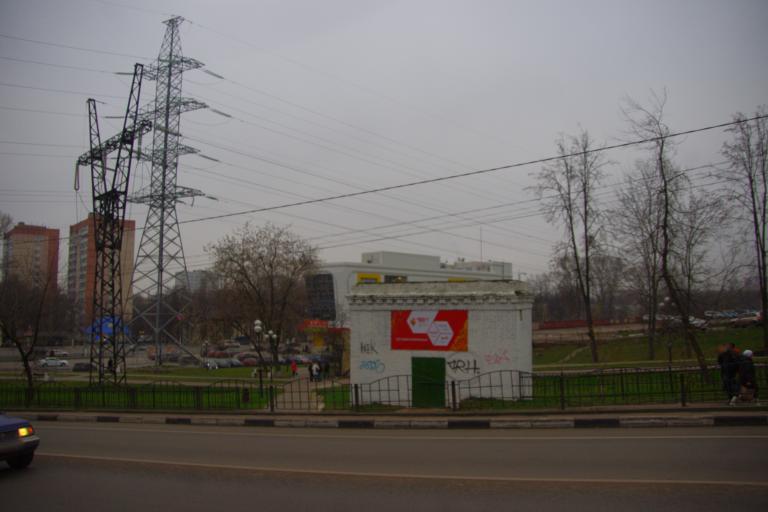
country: RU
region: Moskovskaya
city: Krasnogorsk
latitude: 55.8202
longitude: 37.3400
